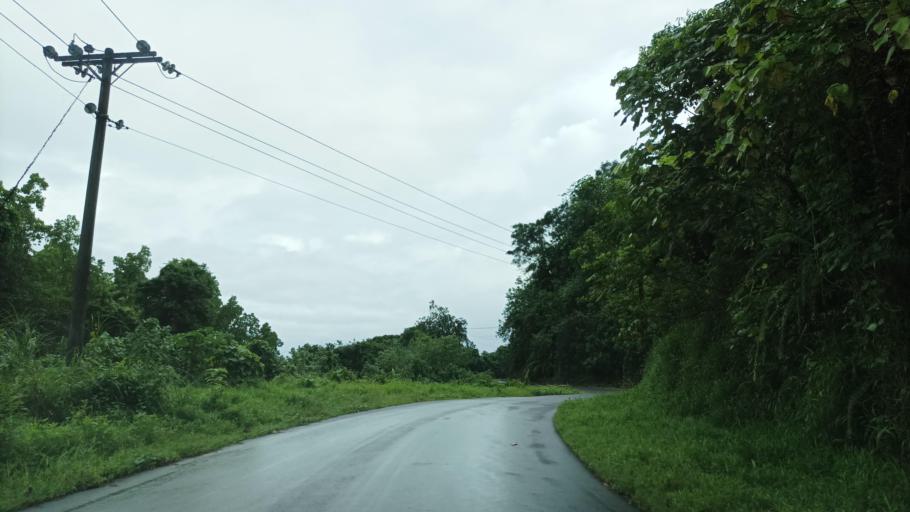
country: FM
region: Pohnpei
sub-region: Madolenihm Municipality
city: Madolenihm Municipality Government
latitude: 6.9153
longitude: 158.3033
